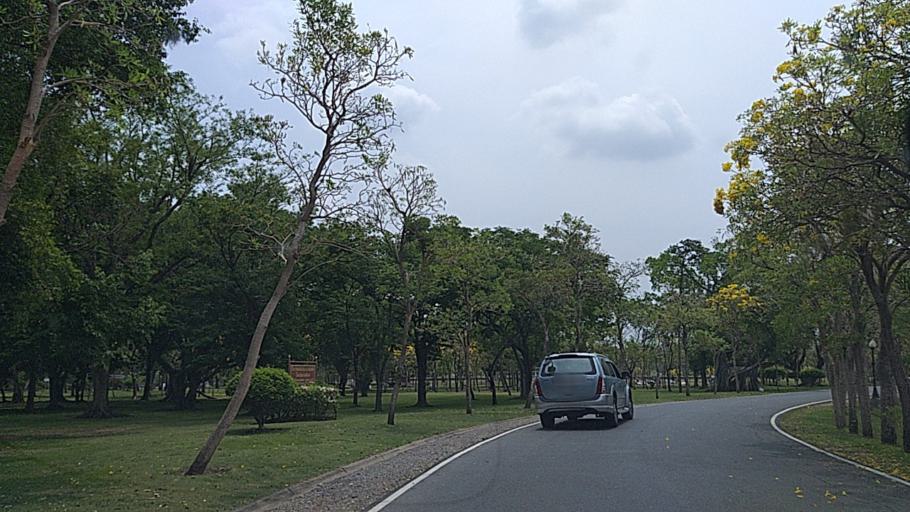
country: TH
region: Bangkok
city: Thawi Watthana
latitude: 13.7800
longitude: 100.3219
